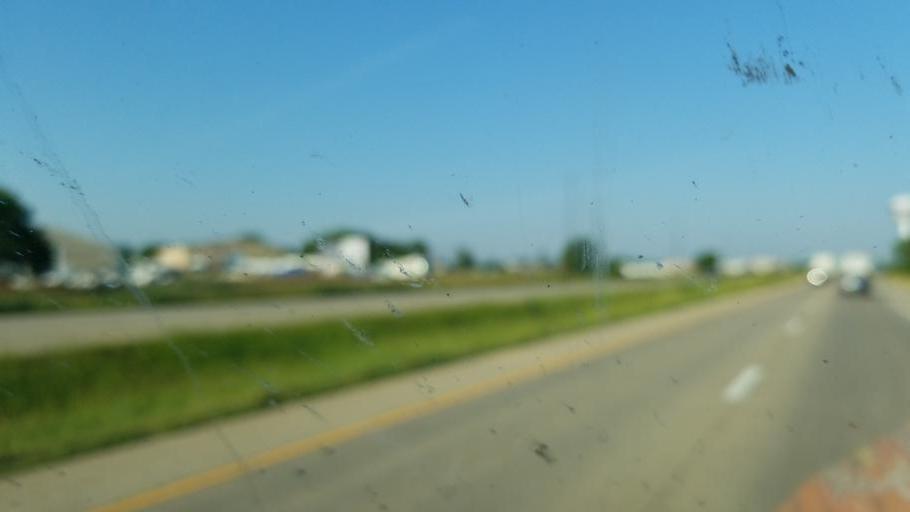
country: US
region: Illinois
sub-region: Grundy County
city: Morris
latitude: 41.3953
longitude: -88.4108
